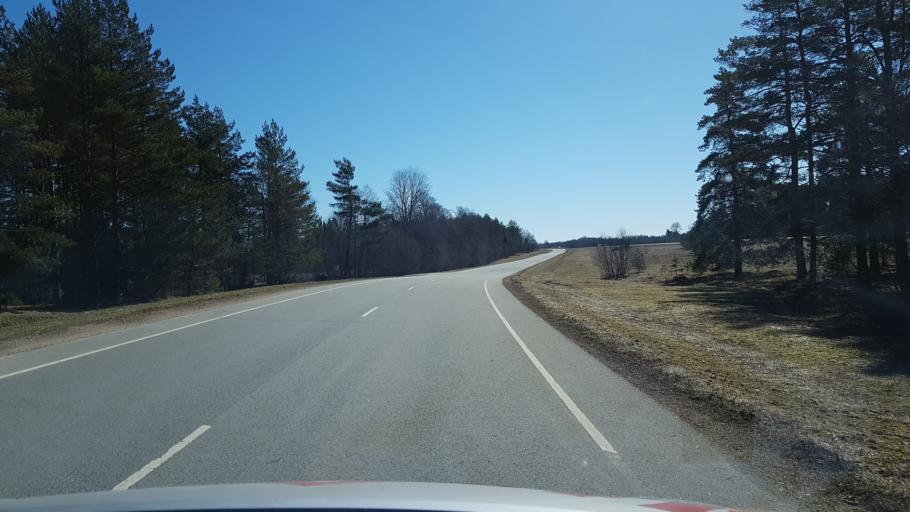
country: EE
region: Laeaene-Virumaa
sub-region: Kadrina vald
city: Kadrina
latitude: 59.4486
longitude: 26.0796
